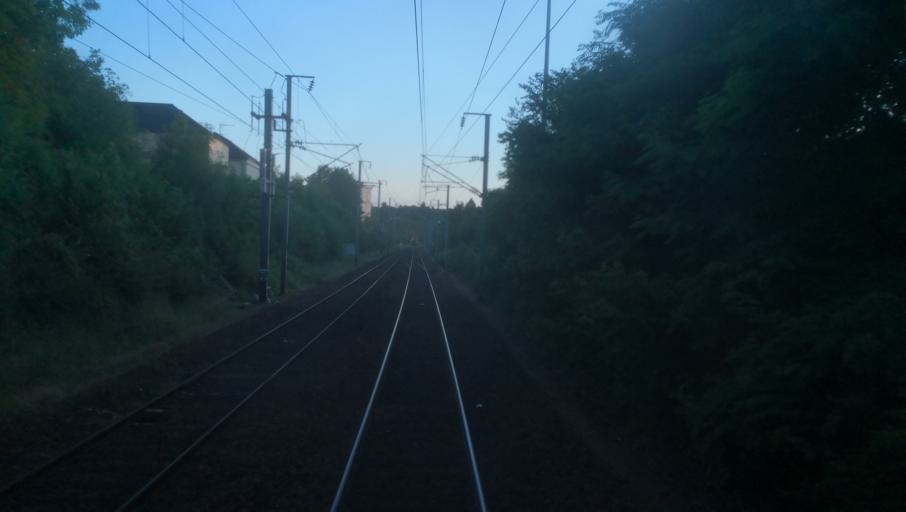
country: FR
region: Haute-Normandie
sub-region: Departement de l'Eure
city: Evreux
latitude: 49.0219
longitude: 1.1606
